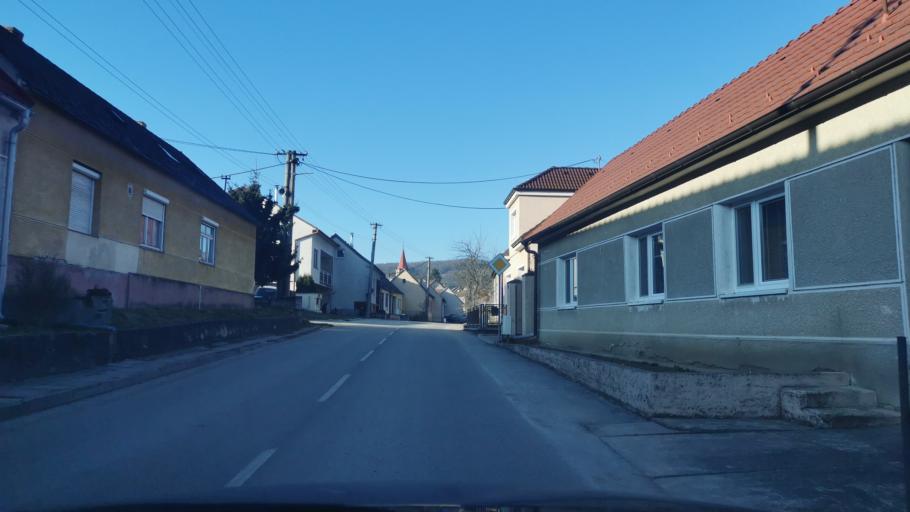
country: SK
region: Trnavsky
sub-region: Okres Senica
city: Senica
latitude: 48.7460
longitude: 17.3540
